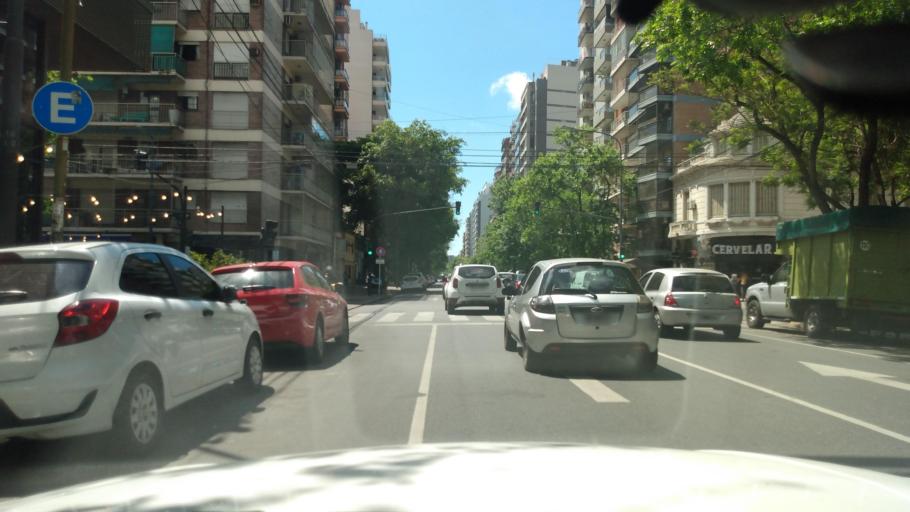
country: AR
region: Buenos Aires F.D.
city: Colegiales
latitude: -34.5749
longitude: -58.4832
